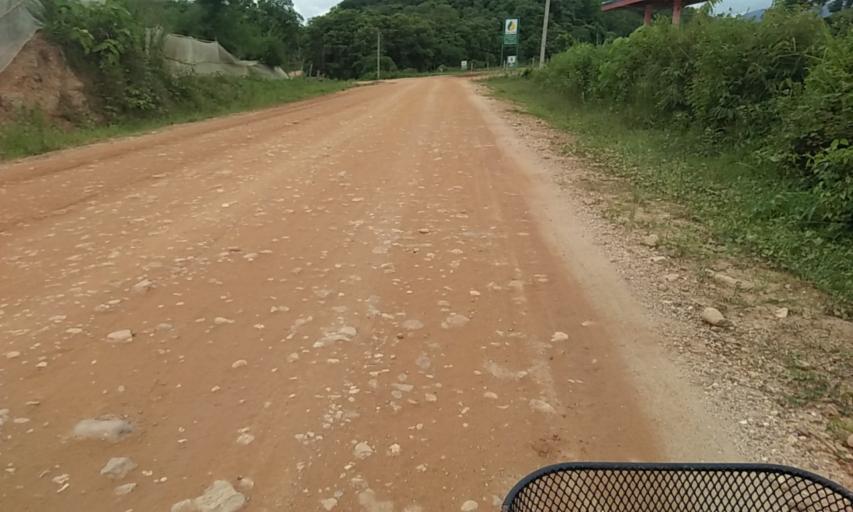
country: TH
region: Nan
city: Chaloem Phra Kiat
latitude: 19.6823
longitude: 100.8101
